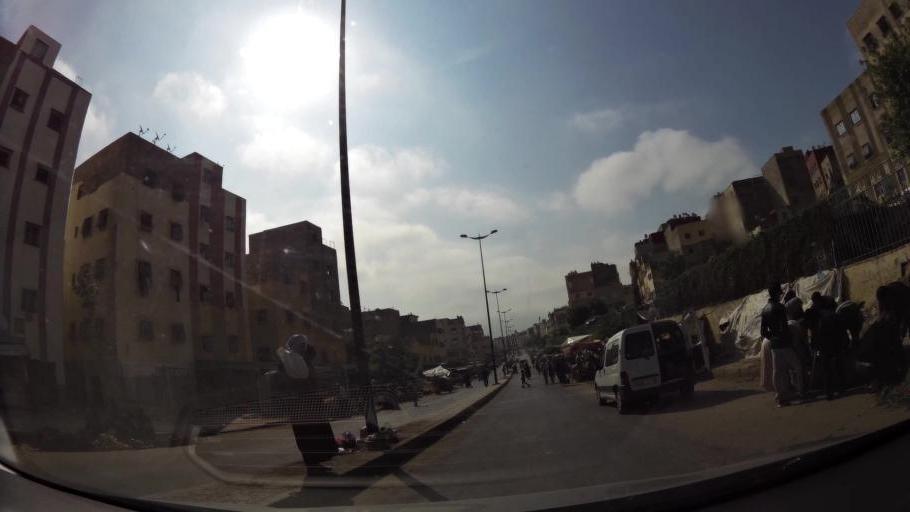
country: MA
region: Fes-Boulemane
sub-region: Fes
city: Fes
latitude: 34.0693
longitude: -5.0092
